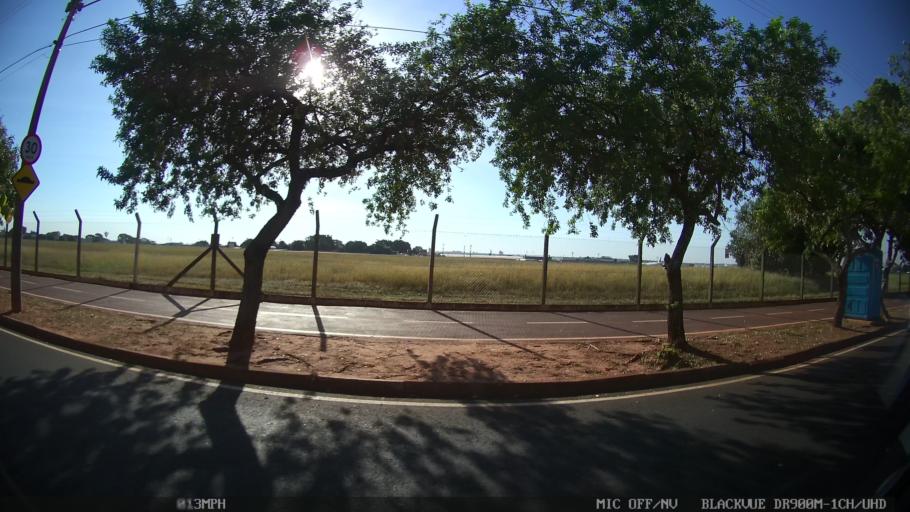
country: BR
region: Sao Paulo
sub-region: Sao Jose Do Rio Preto
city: Sao Jose do Rio Preto
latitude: -20.8161
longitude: -49.4031
